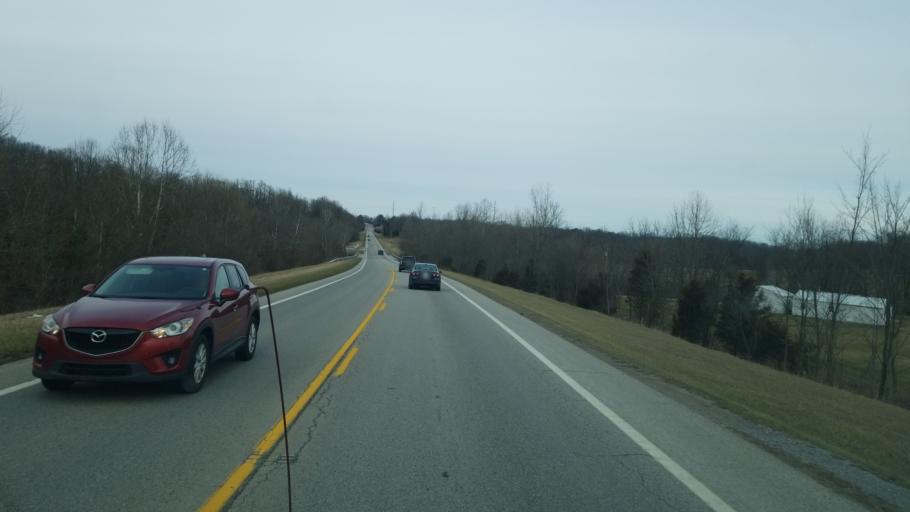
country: US
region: Ohio
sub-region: Highland County
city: Hillsboro
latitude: 39.1732
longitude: -83.6231
